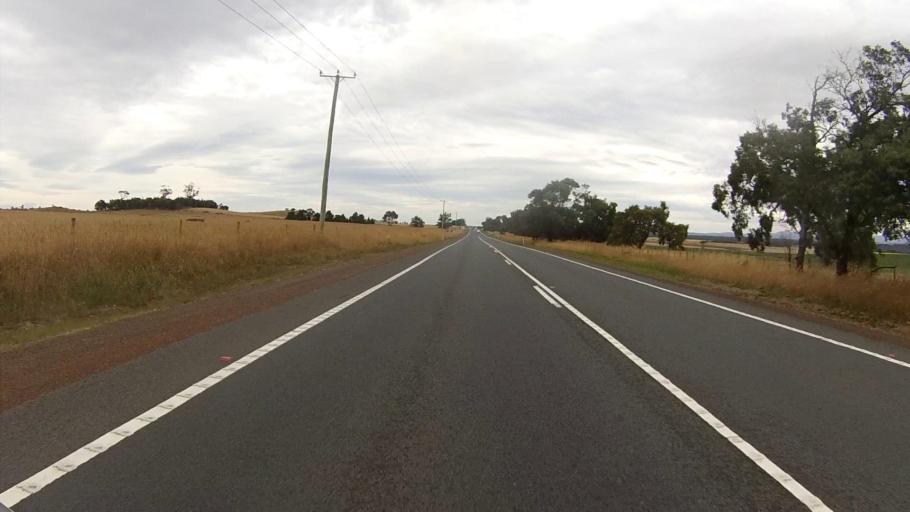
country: AU
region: Tasmania
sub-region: Northern Midlands
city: Evandale
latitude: -41.9103
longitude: 147.4814
